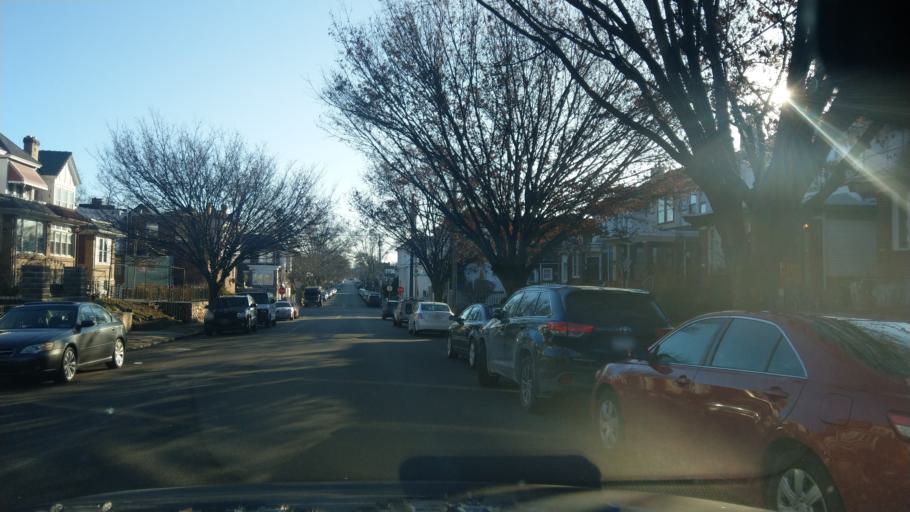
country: US
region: Pennsylvania
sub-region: Montgomery County
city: Wyncote
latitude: 40.0568
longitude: -75.1475
